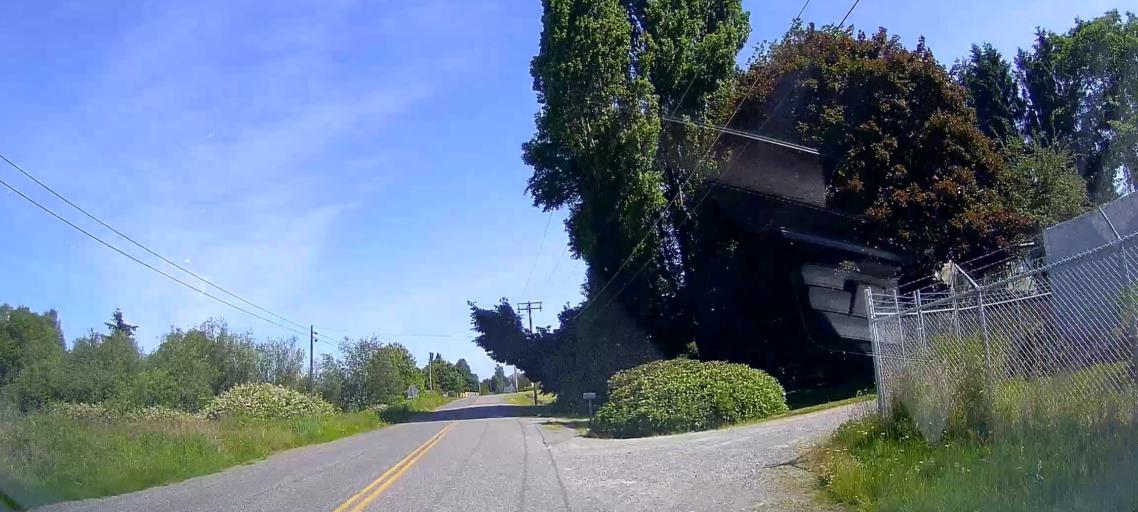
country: US
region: Washington
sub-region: Skagit County
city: Burlington
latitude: 48.4833
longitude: -122.3084
